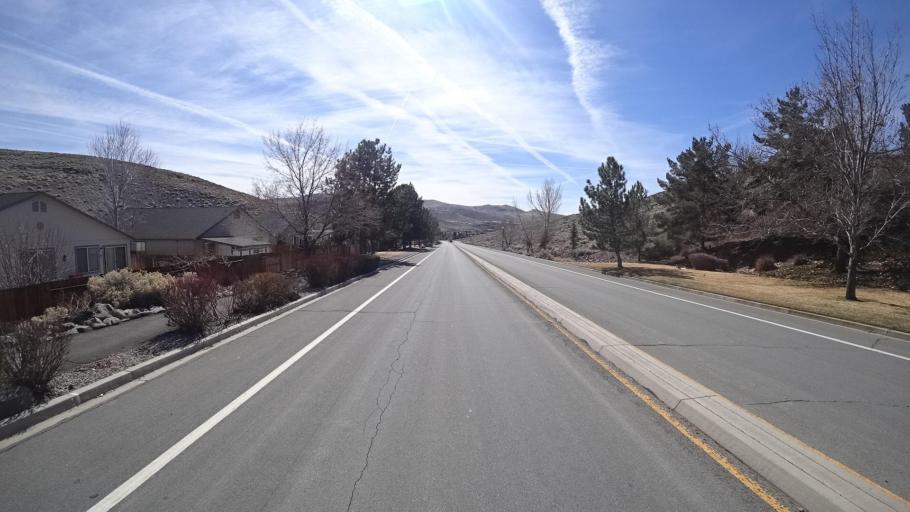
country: US
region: Nevada
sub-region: Washoe County
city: Sparks
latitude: 39.5761
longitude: -119.6972
